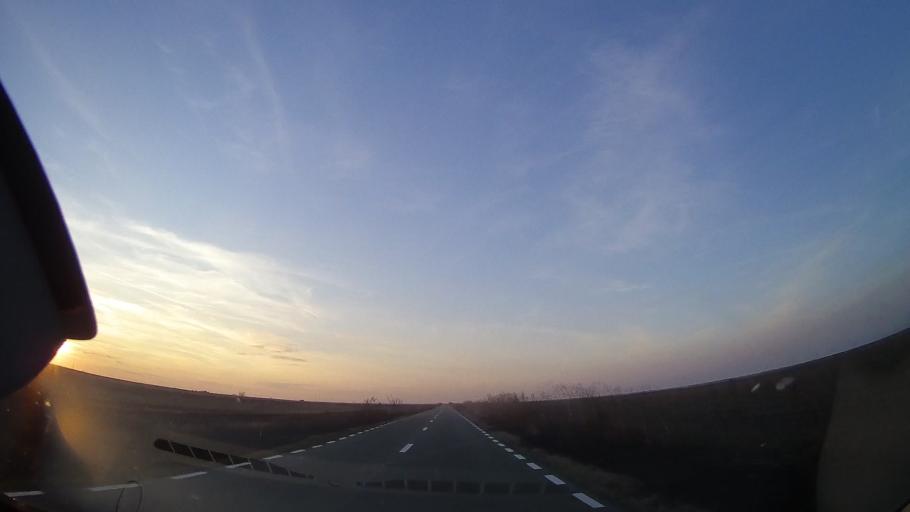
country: RO
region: Constanta
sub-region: Comuna Topraisar
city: Topraisar
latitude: 44.0210
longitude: 28.4164
